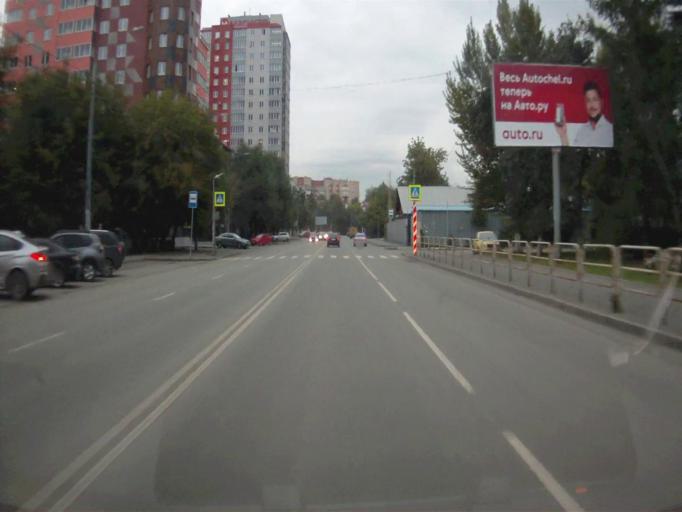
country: RU
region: Chelyabinsk
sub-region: Gorod Chelyabinsk
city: Chelyabinsk
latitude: 55.1511
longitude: 61.3985
